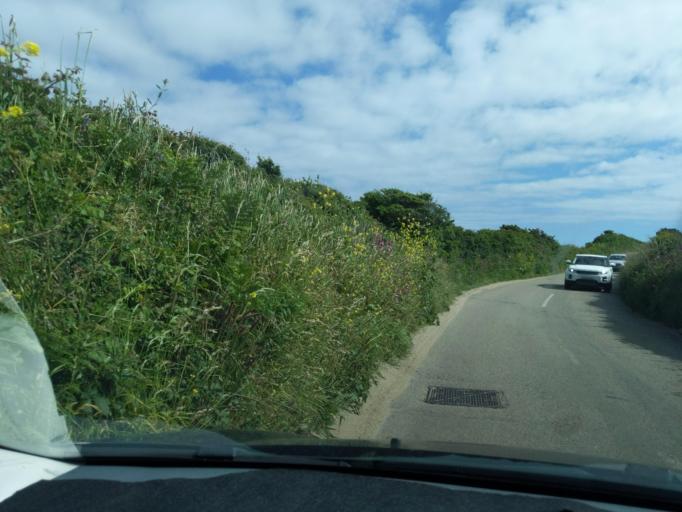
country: GB
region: England
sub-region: Cornwall
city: St. Buryan
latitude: 50.0650
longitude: -5.6343
